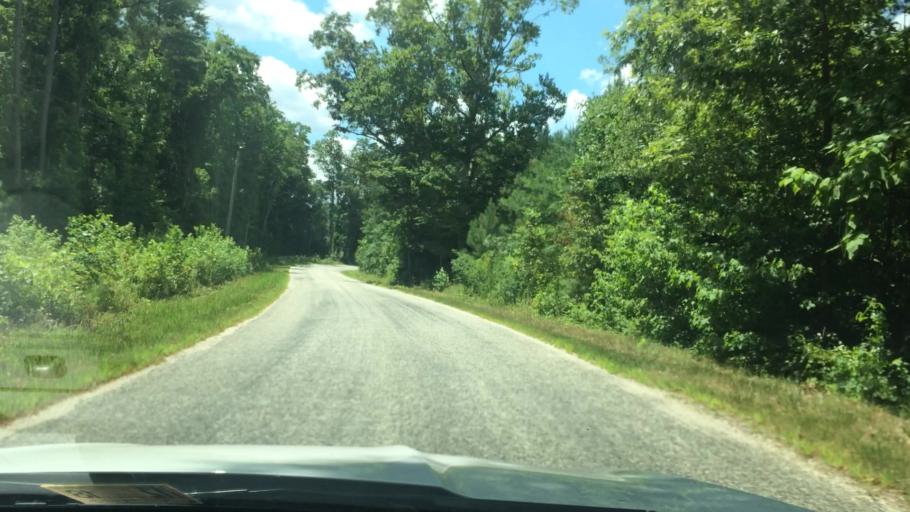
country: US
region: Virginia
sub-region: King William County
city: West Point
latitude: 37.6054
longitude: -76.7833
